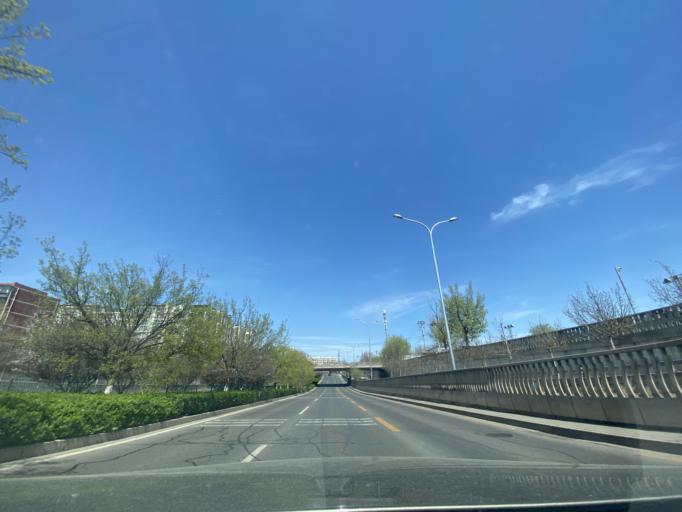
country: CN
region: Beijing
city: Sijiqing
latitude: 39.9303
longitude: 116.2470
